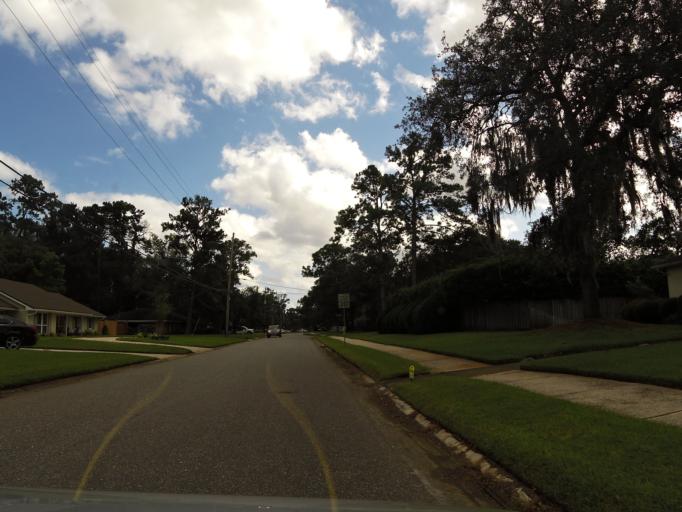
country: US
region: Florida
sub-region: Duval County
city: Jacksonville
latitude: 30.2571
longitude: -81.7013
